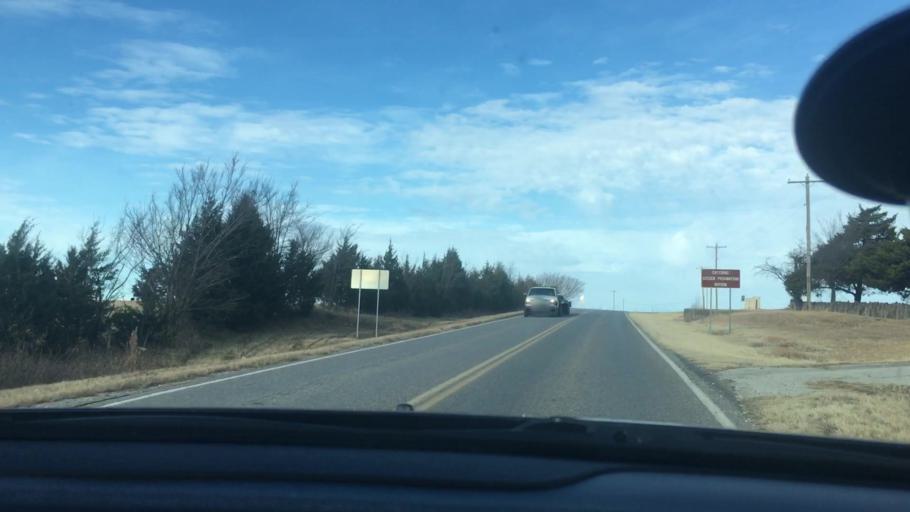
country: US
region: Oklahoma
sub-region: Seminole County
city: Konawa
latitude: 34.9694
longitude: -96.7756
